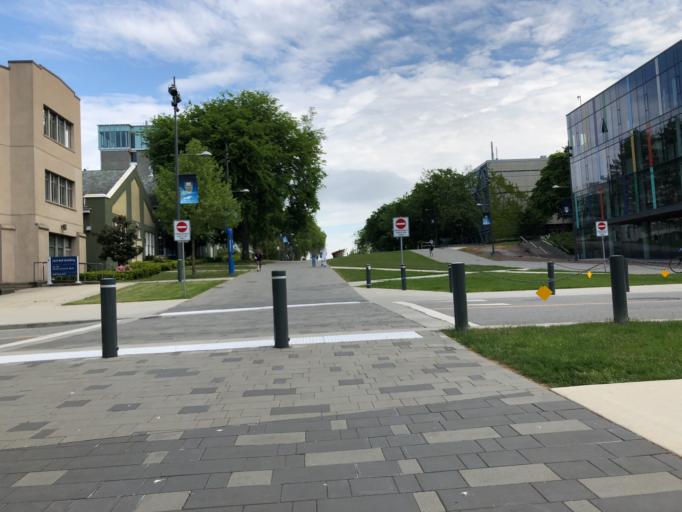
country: CA
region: British Columbia
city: West End
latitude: 49.2640
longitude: -123.2551
